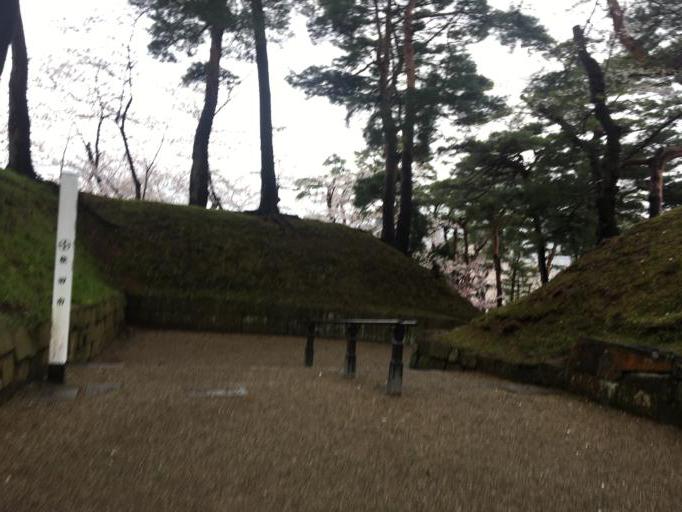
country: JP
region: Akita
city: Akita
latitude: 39.7209
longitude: 140.1241
